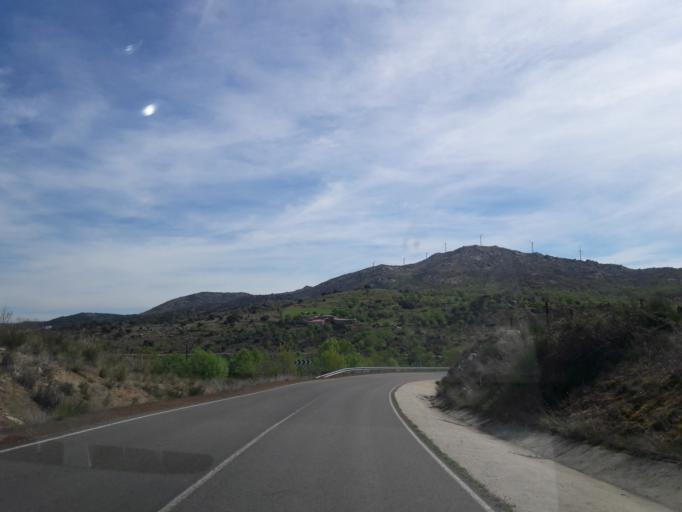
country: ES
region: Castille and Leon
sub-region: Provincia de Salamanca
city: Sanchotello
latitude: 40.4434
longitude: -5.7414
